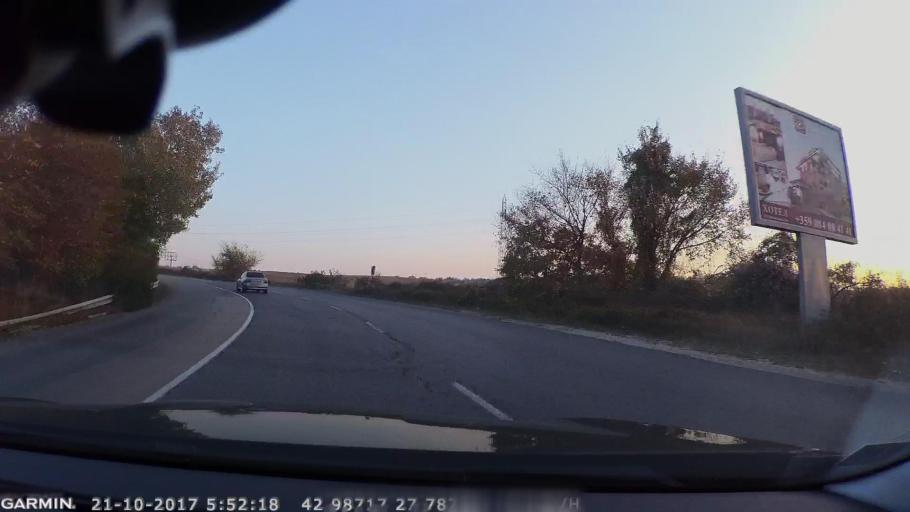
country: BG
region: Varna
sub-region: Obshtina Dolni Chiflik
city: Dolni Chiflik
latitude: 42.9863
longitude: 27.7884
